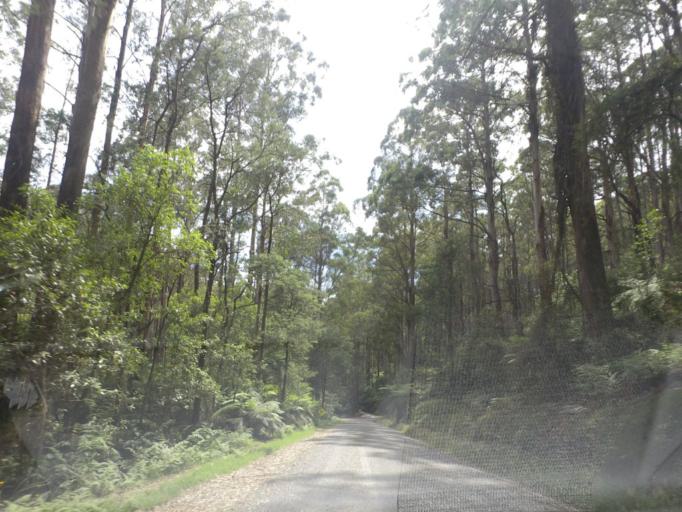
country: AU
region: Victoria
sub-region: Yarra Ranges
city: Healesville
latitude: -37.5294
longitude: 145.5180
